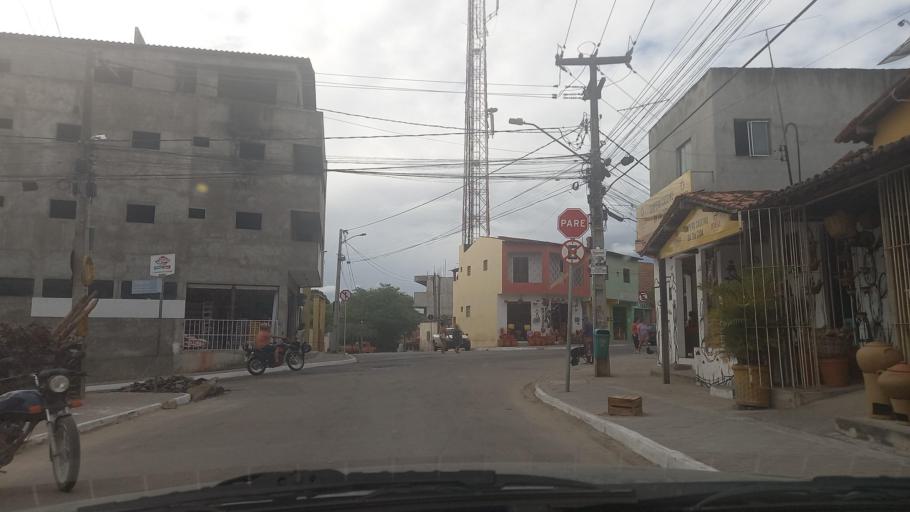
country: BR
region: Pernambuco
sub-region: Caruaru
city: Caruaru
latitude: -8.2920
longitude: -36.0304
